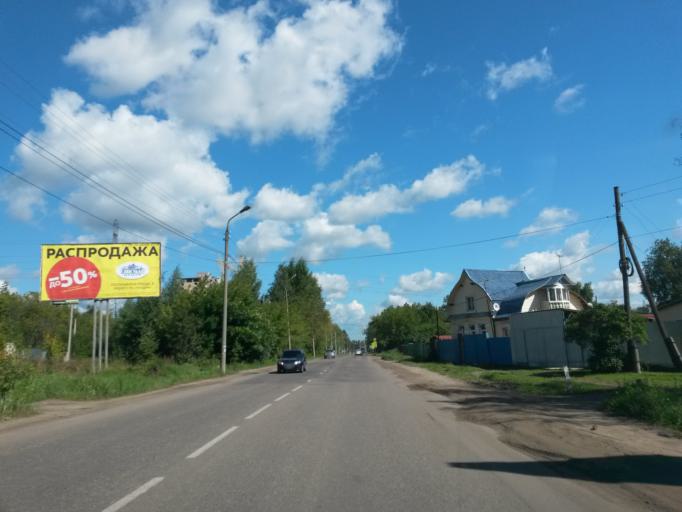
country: RU
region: Jaroslavl
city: Yaroslavl
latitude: 57.5819
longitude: 39.8717
